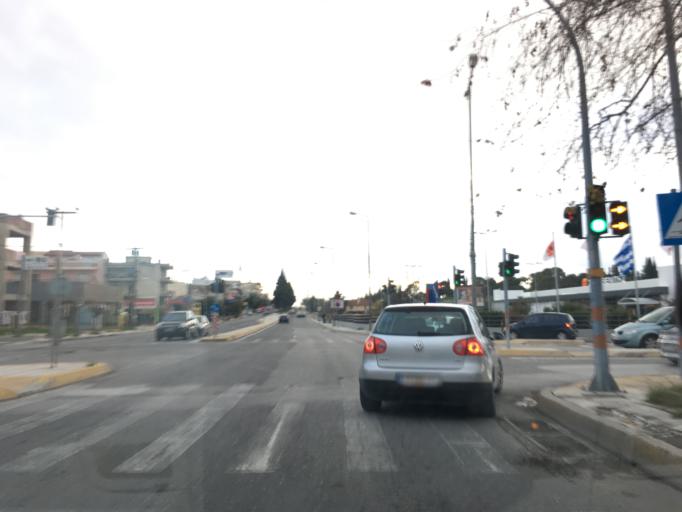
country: GR
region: Attica
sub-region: Nomarchia Athinas
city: Agioi Anargyroi
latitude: 38.0424
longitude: 23.7267
